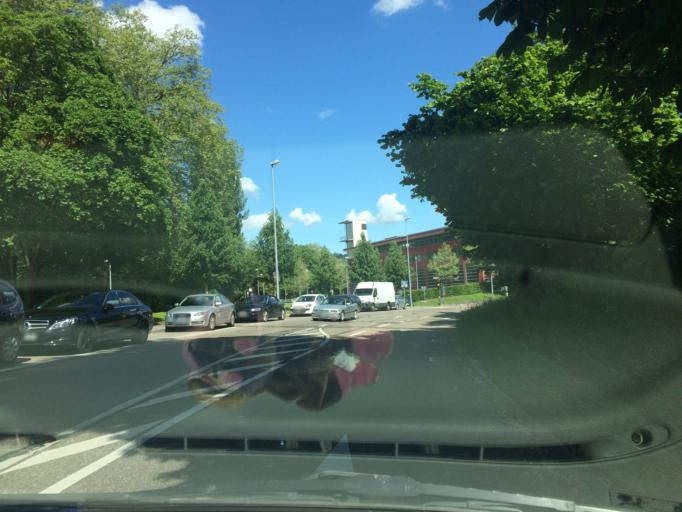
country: DE
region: Baden-Wuerttemberg
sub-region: Regierungsbezirk Stuttgart
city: Esslingen
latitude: 48.7331
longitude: 9.3139
